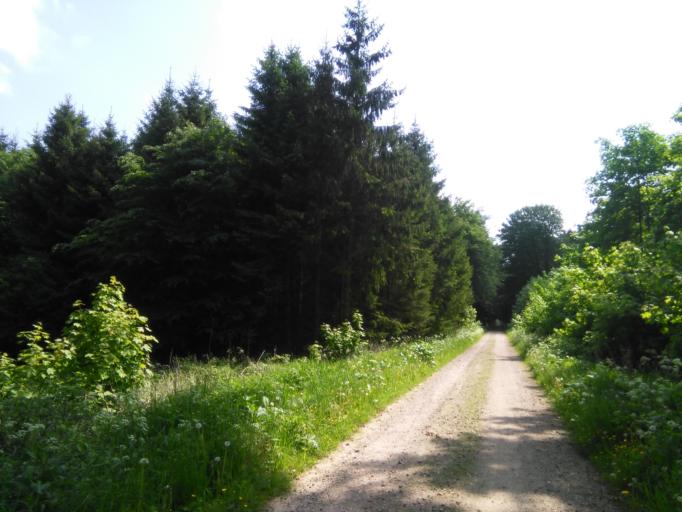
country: DK
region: Central Jutland
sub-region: Favrskov Kommune
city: Hinnerup
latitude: 56.2631
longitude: 10.0455
